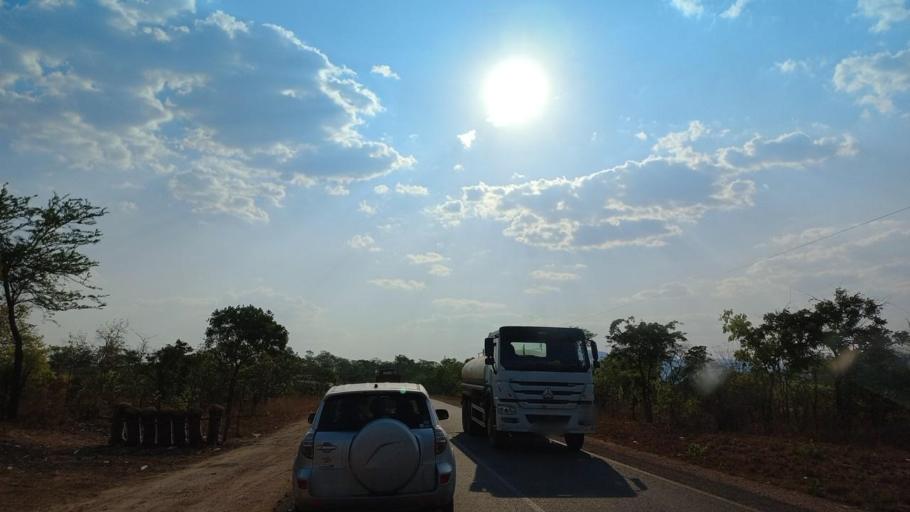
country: ZM
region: Lusaka
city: Luangwa
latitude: -14.9781
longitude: 29.9941
